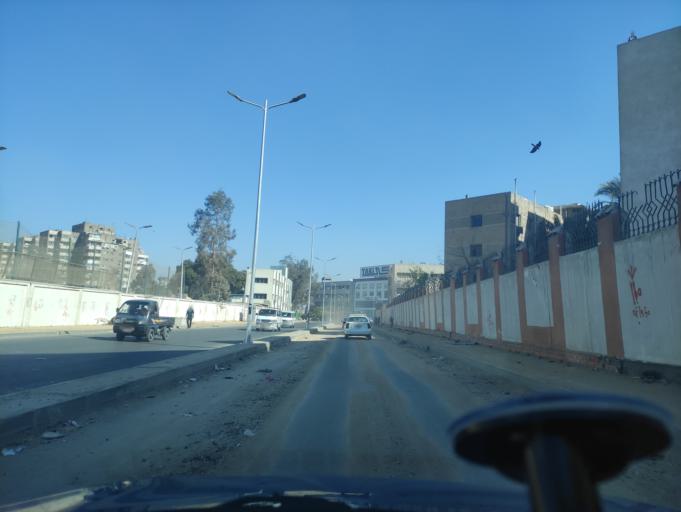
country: EG
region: Muhafazat al Qahirah
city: Cairo
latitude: 30.0573
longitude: 31.2766
